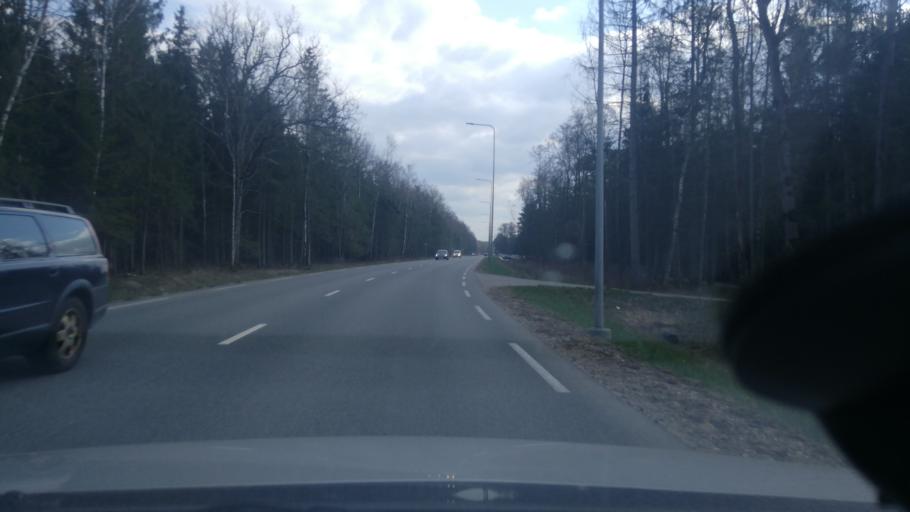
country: LT
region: Klaipedos apskritis
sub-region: Klaipeda
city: Klaipeda
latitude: 55.7518
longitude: 21.0913
